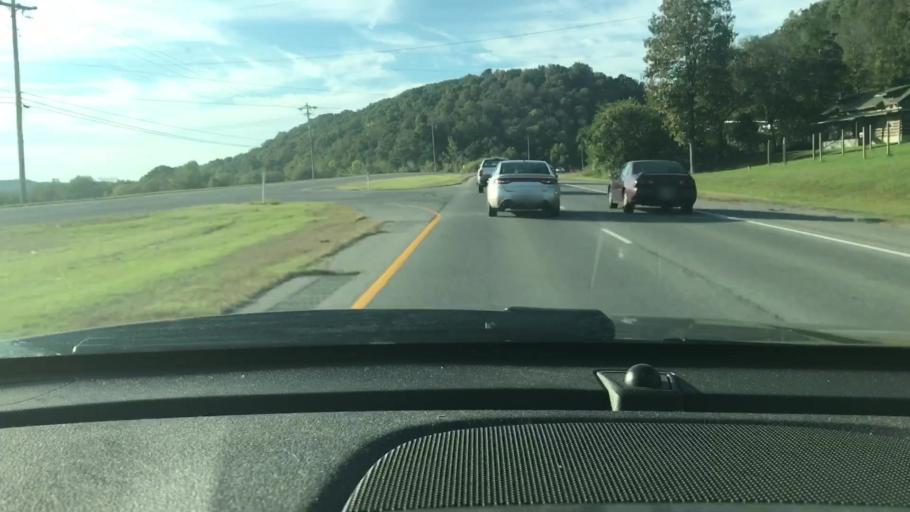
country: US
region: Tennessee
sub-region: Cheatham County
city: Ashland City
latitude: 36.2304
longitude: -87.0160
